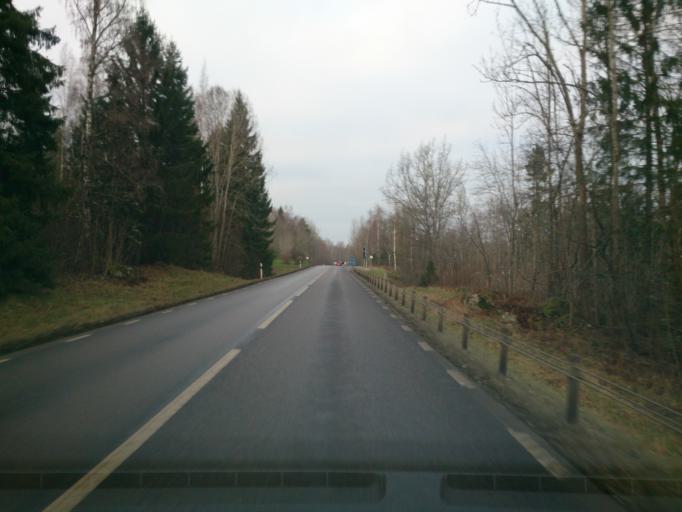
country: SE
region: OEstergoetland
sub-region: Atvidabergs Kommun
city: Atvidaberg
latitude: 58.2470
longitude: 15.9321
